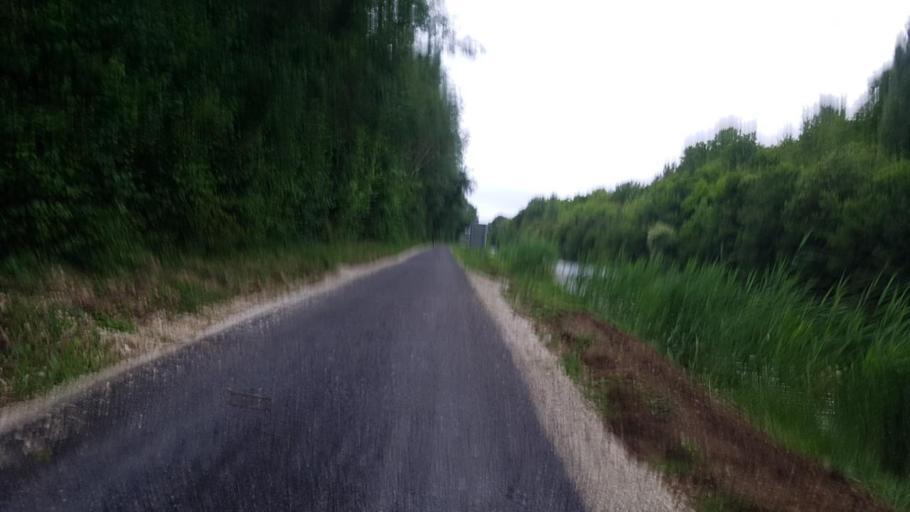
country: FR
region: Champagne-Ardenne
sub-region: Departement de la Marne
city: Sarry
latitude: 48.8406
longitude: 4.5021
